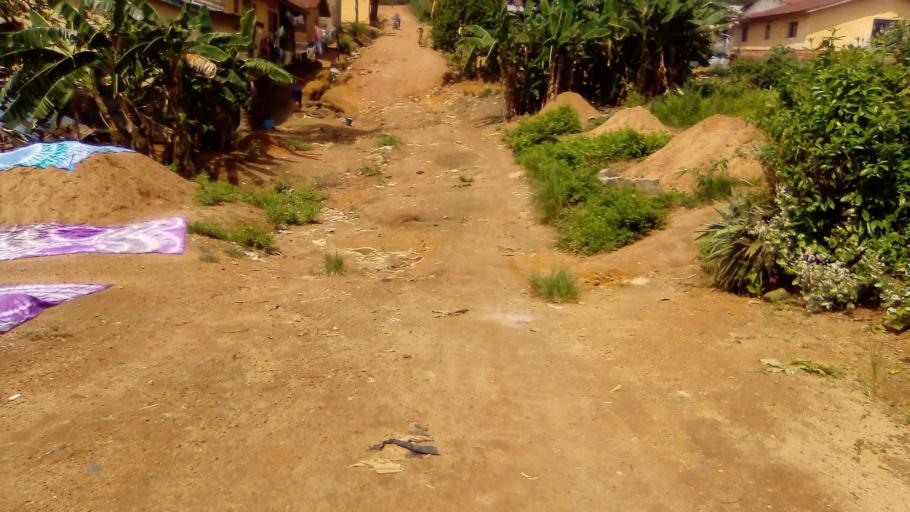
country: SL
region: Southern Province
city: Bo
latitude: 7.9787
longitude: -11.7409
